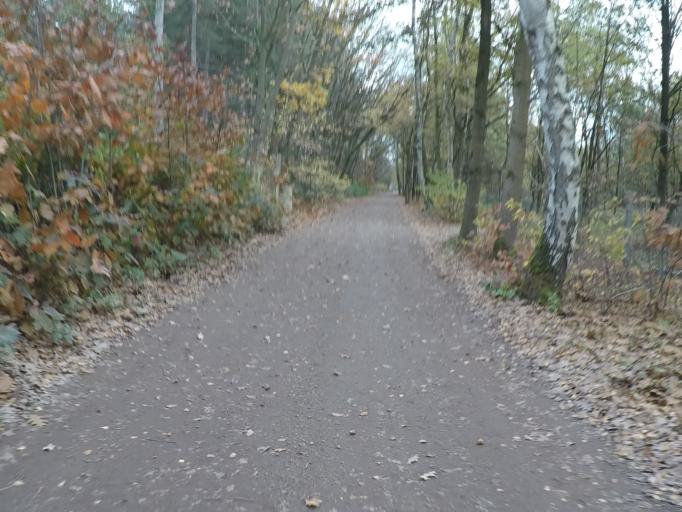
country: BE
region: Flanders
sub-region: Provincie Antwerpen
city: Nijlen
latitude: 51.1640
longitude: 4.6399
